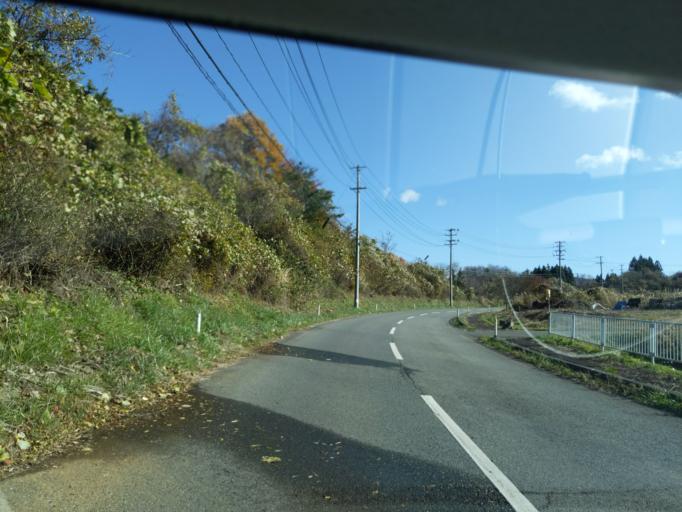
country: JP
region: Iwate
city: Mizusawa
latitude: 39.0283
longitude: 141.1097
